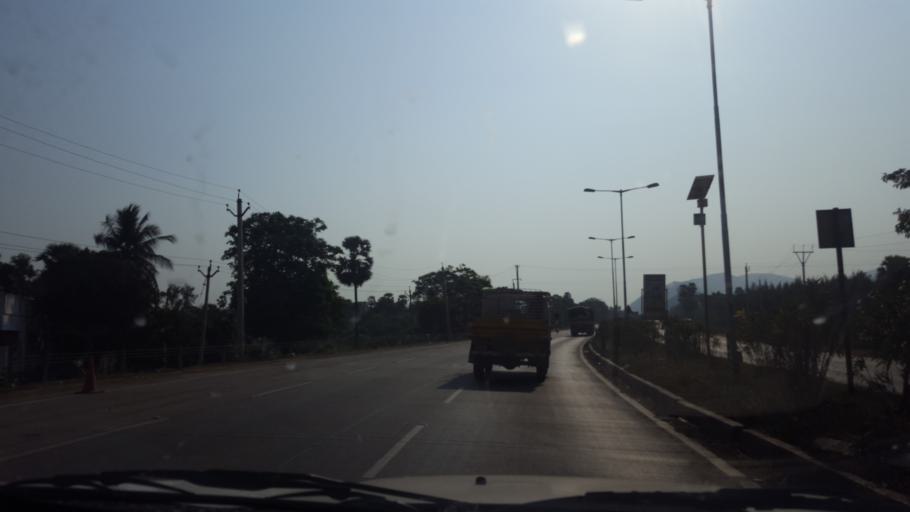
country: IN
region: Andhra Pradesh
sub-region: Vishakhapatnam
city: Elamanchili
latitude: 17.5643
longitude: 82.8609
